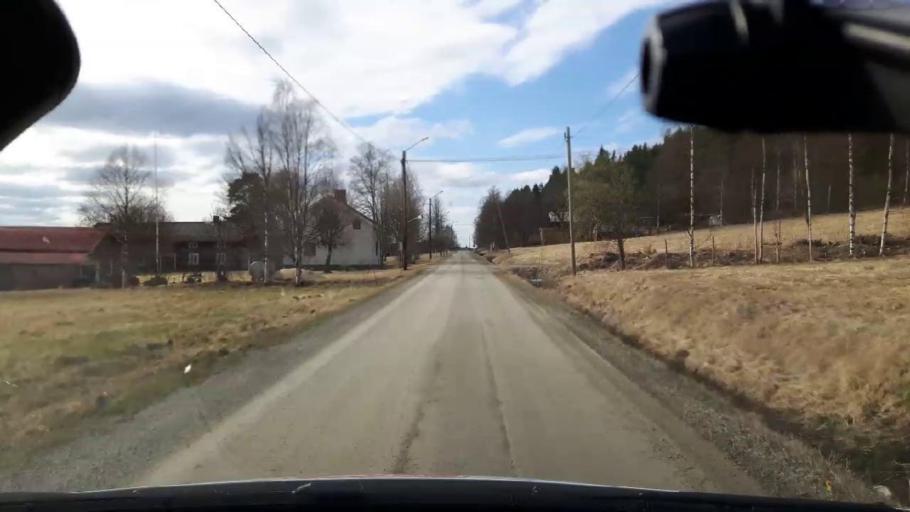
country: SE
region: Jaemtland
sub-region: Bergs Kommun
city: Hoverberg
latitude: 62.7144
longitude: 14.6862
